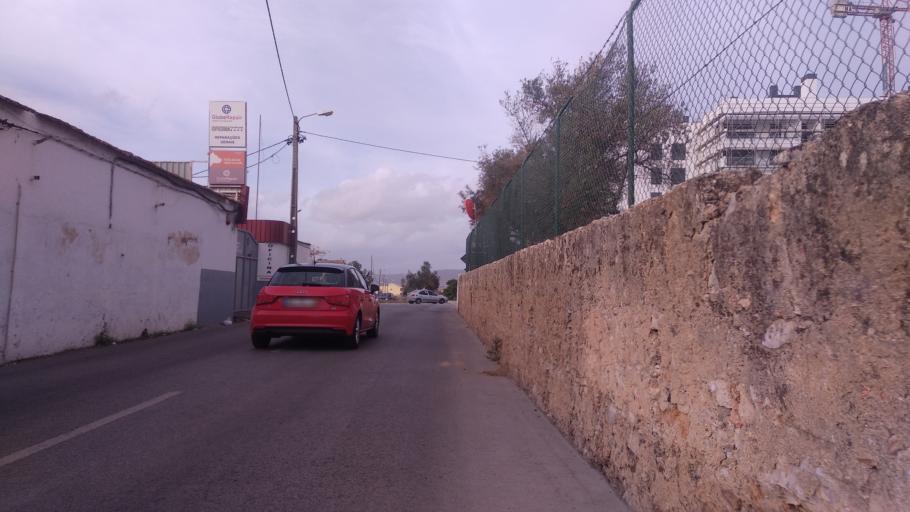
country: PT
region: Faro
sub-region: Faro
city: Faro
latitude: 37.0291
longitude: -7.9397
